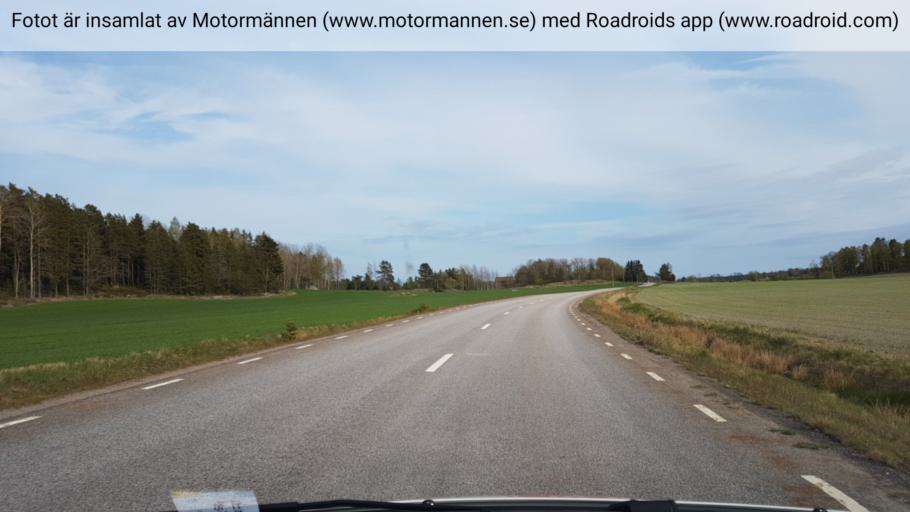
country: SE
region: Kalmar
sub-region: Vasterviks Kommun
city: Forserum
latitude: 57.9399
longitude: 16.4985
